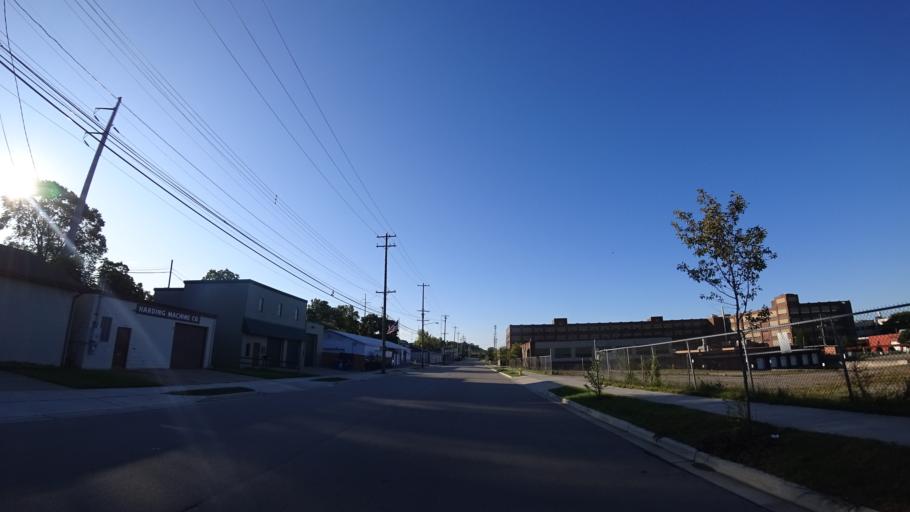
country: US
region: Michigan
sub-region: Kent County
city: Grand Rapids
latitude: 42.9884
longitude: -85.6687
